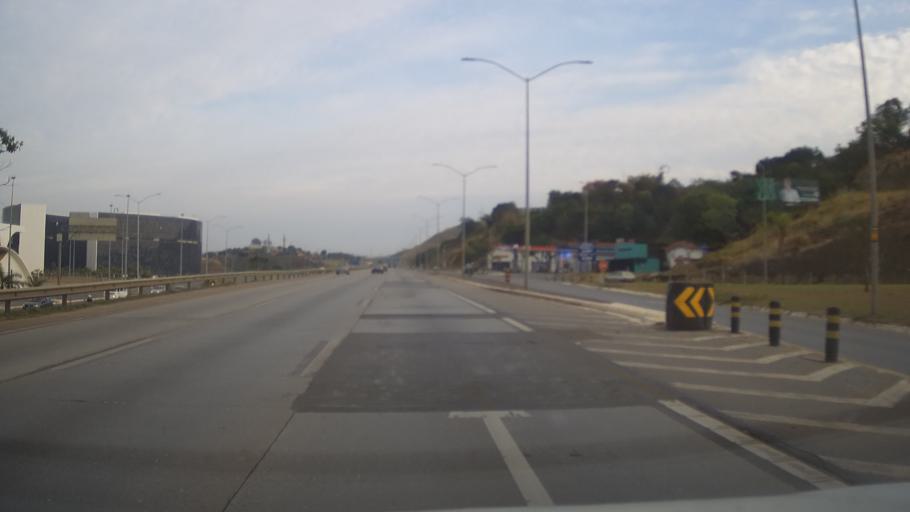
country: BR
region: Minas Gerais
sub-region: Santa Luzia
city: Santa Luzia
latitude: -19.7901
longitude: -43.9489
